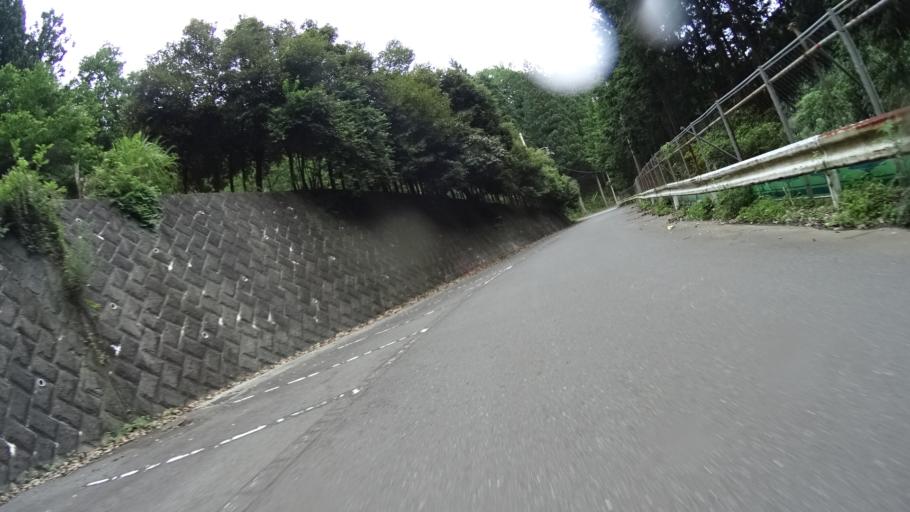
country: JP
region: Kanagawa
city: Hadano
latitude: 35.4866
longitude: 139.2146
